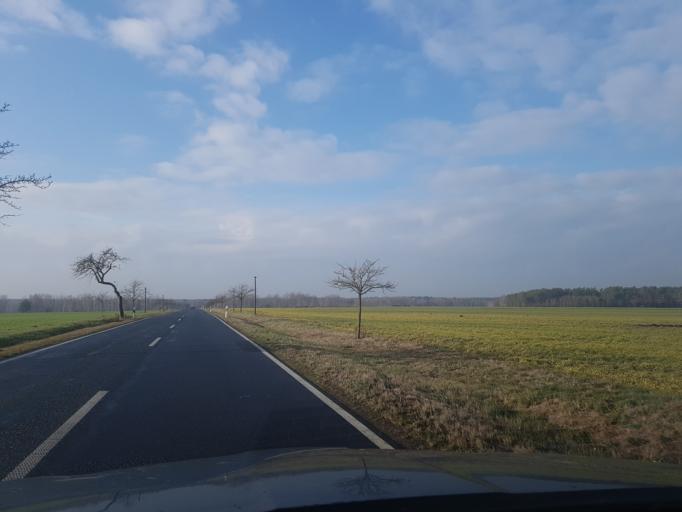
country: DE
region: Brandenburg
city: Ruckersdorf
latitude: 51.5340
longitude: 13.6127
